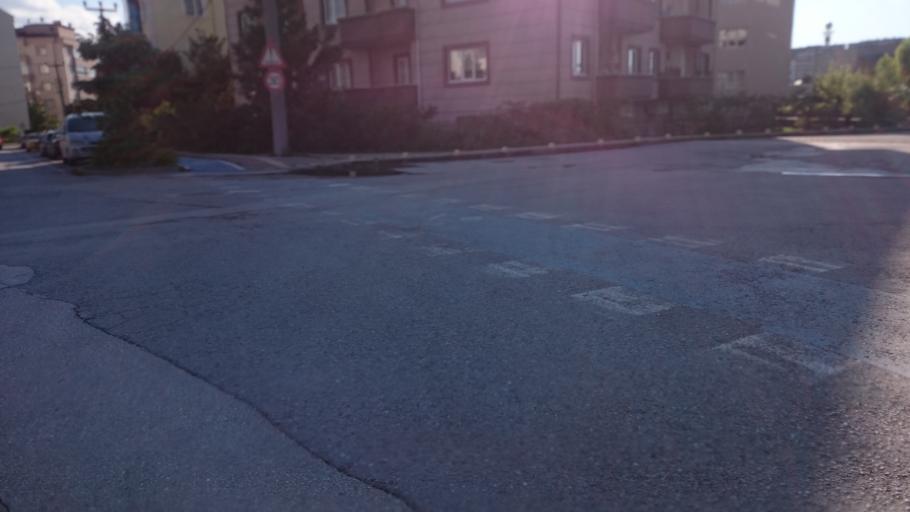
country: TR
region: Bursa
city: Niluefer
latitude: 40.2244
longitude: 28.9681
